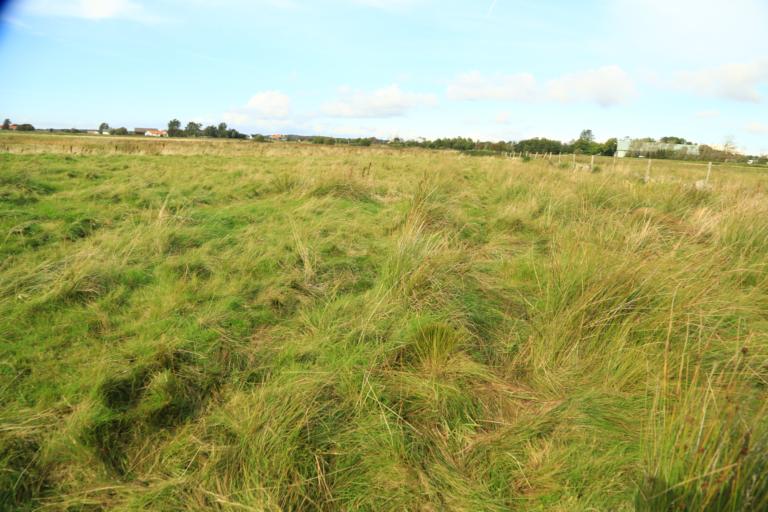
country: SE
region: Halland
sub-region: Varbergs Kommun
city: Traslovslage
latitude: 57.0232
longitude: 12.3332
